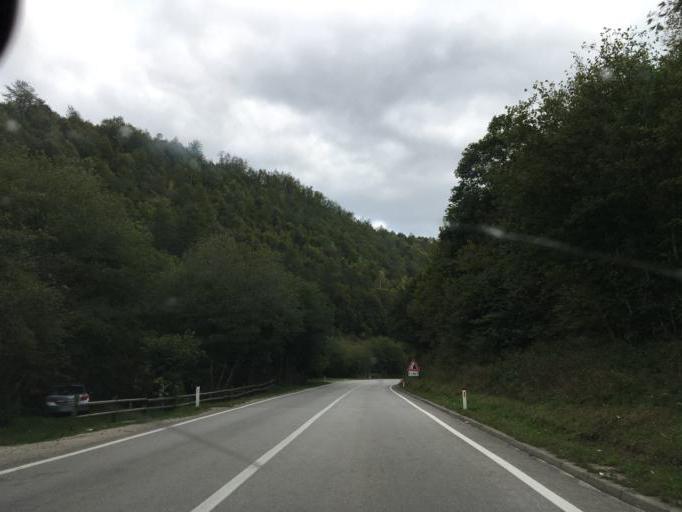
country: BA
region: Federation of Bosnia and Herzegovina
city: Novi Travnik
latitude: 44.0988
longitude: 17.5754
